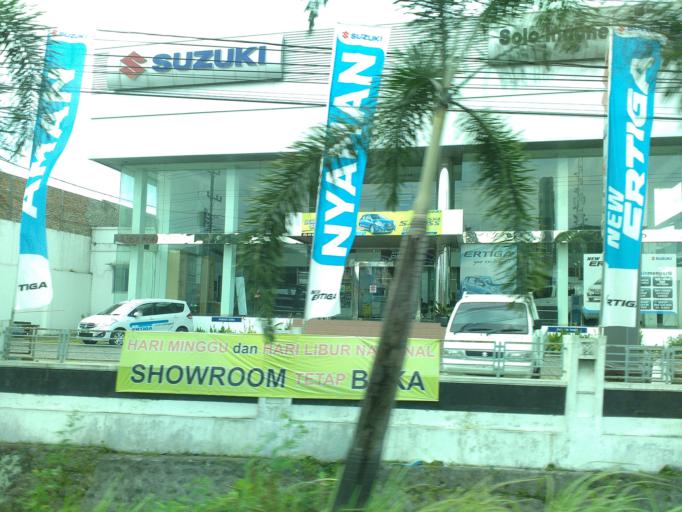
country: ID
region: Central Java
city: Klaten
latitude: -7.6869
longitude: 110.6362
